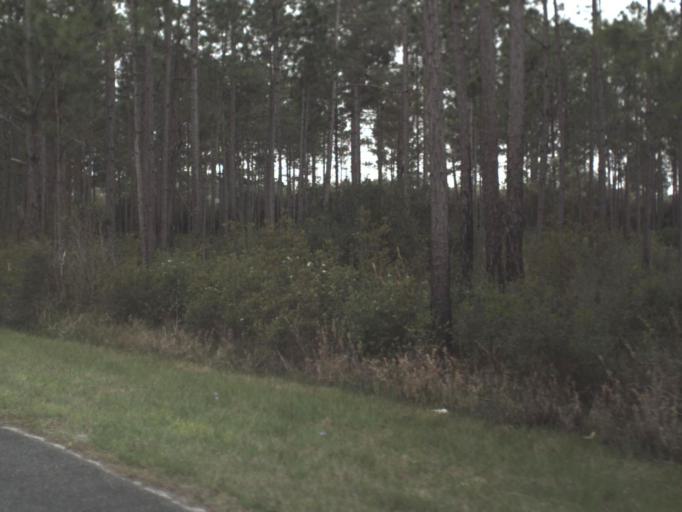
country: US
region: Florida
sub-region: Franklin County
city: Eastpoint
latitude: 29.7858
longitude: -84.8313
